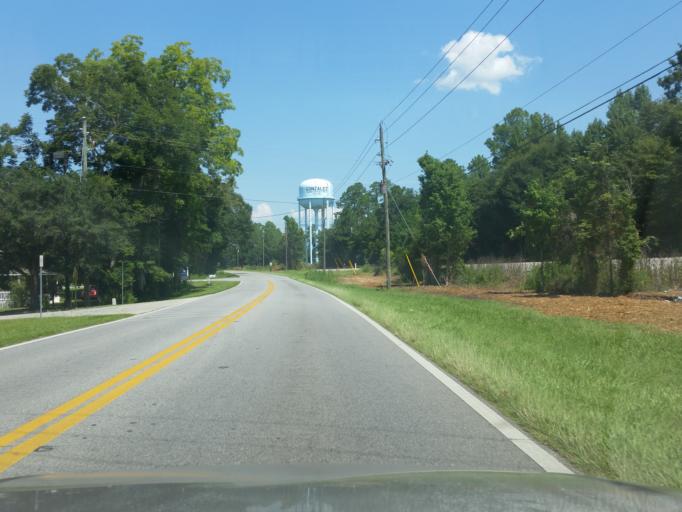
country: US
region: Florida
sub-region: Escambia County
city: Gonzalez
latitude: 30.5812
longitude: -87.2953
